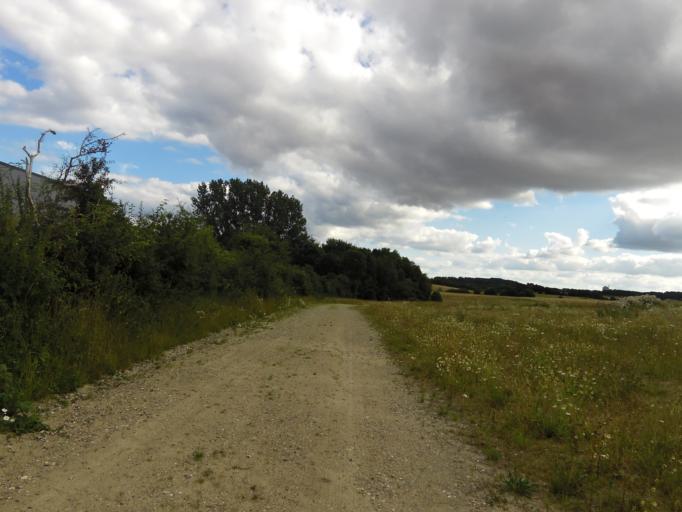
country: DK
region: South Denmark
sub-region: Haderslev Kommune
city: Haderslev
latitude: 55.2355
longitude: 9.4850
